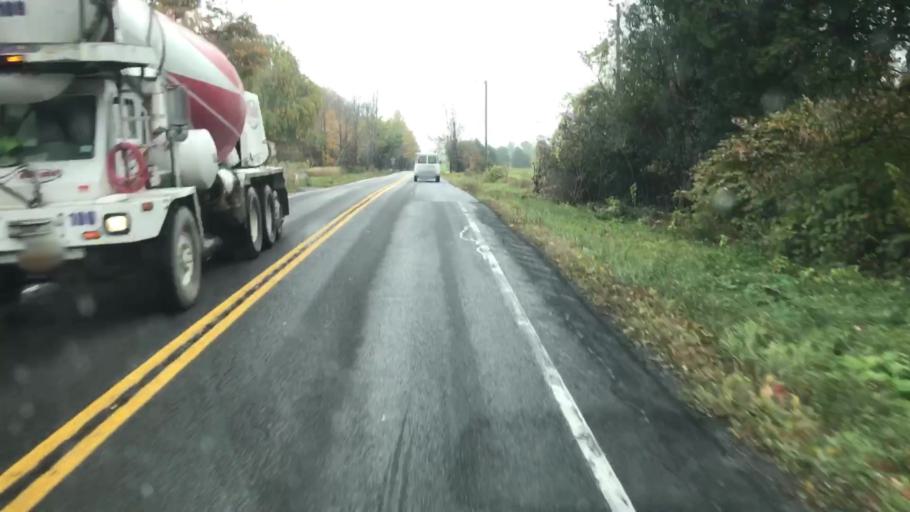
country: US
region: New York
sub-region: Onondaga County
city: Skaneateles
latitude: 42.9816
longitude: -76.4282
